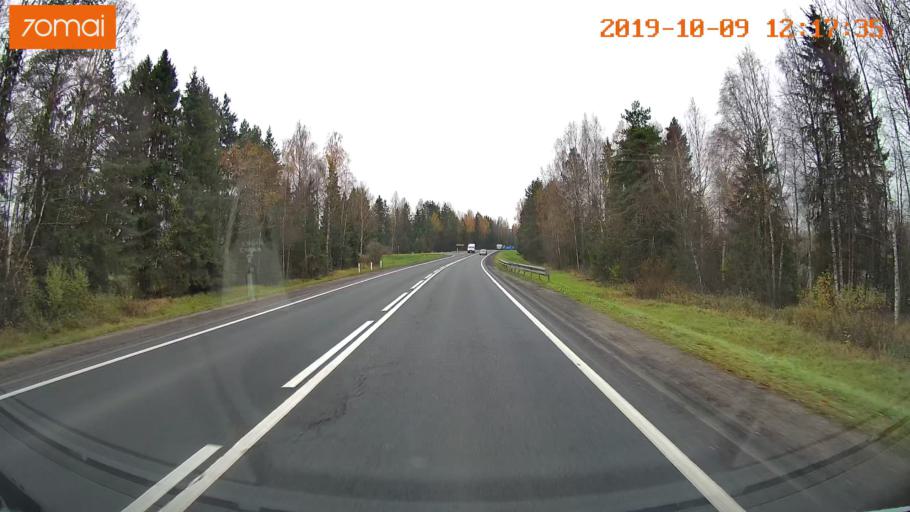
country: RU
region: Jaroslavl
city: Prechistoye
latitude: 58.4543
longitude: 40.3216
